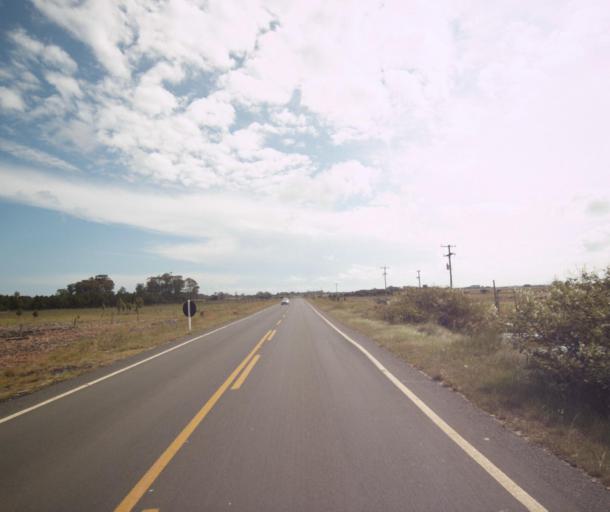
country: BR
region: Rio Grande do Sul
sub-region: Sao Lourenco Do Sul
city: Sao Lourenco do Sul
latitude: -31.6086
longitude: -51.3902
